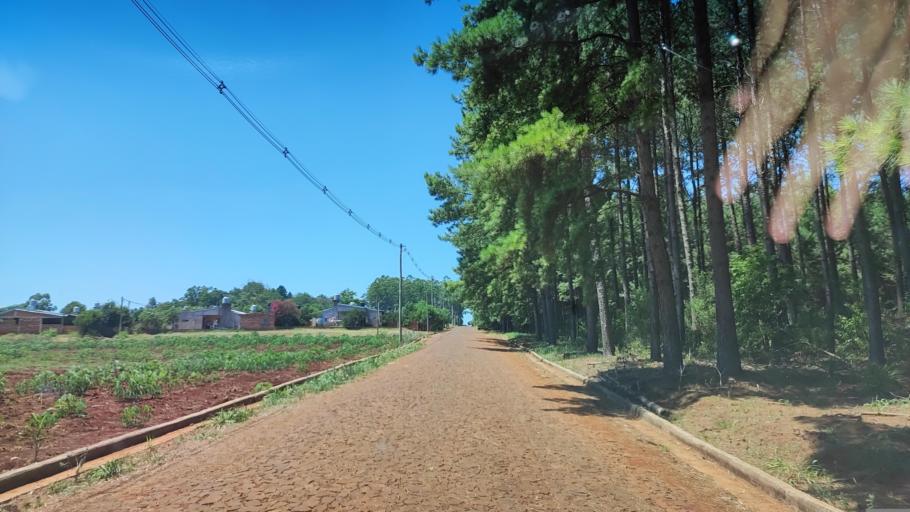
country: AR
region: Misiones
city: Capiovi
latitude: -26.9270
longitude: -55.0668
